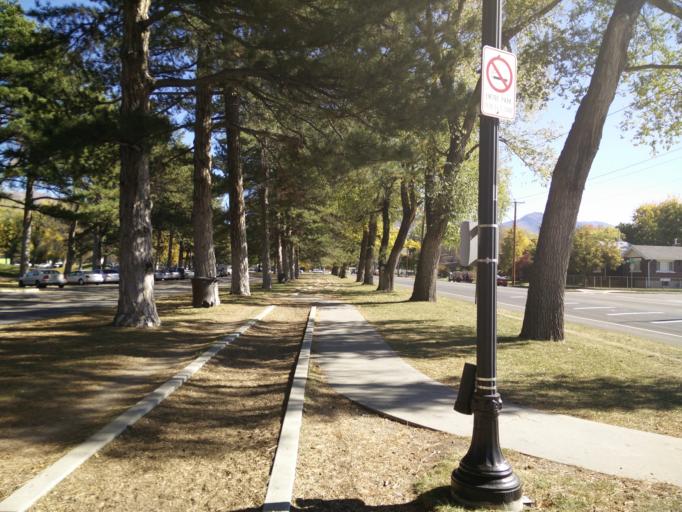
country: US
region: Utah
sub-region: Salt Lake County
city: Salt Lake City
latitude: 40.7418
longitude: -111.8738
